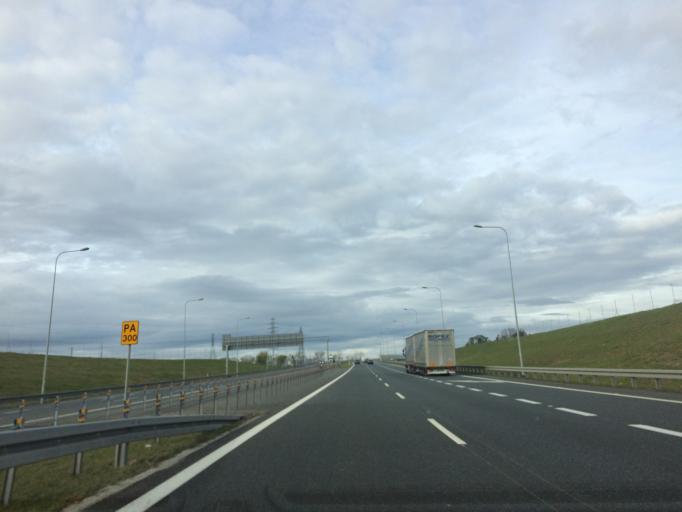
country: PL
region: Lower Silesian Voivodeship
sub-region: Legnica
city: Legnica
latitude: 51.1759
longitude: 16.0918
